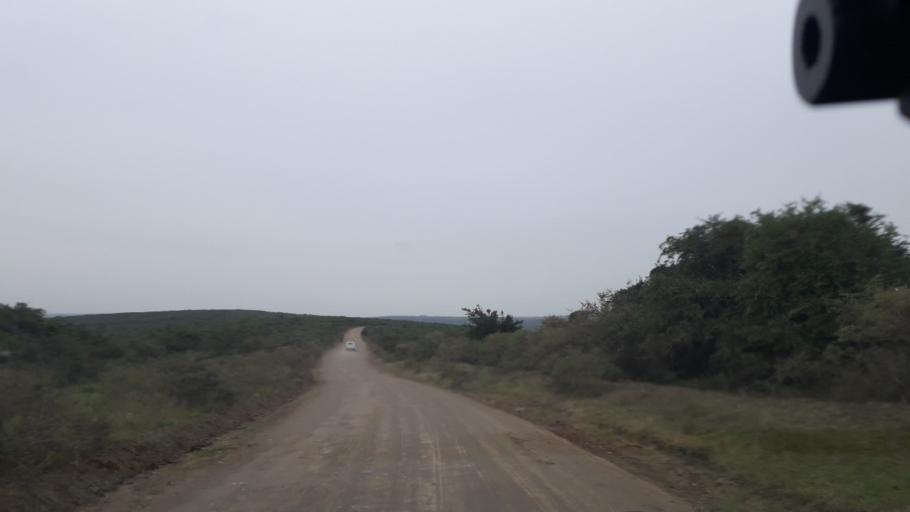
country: ZA
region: Eastern Cape
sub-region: Buffalo City Metropolitan Municipality
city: Bhisho
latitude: -32.7913
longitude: 27.3309
